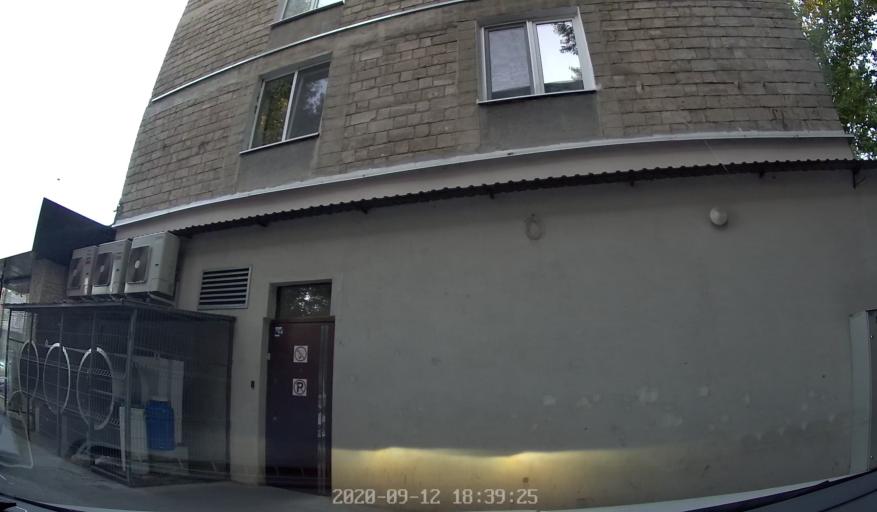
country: MD
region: Chisinau
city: Chisinau
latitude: 46.9979
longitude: 28.8581
